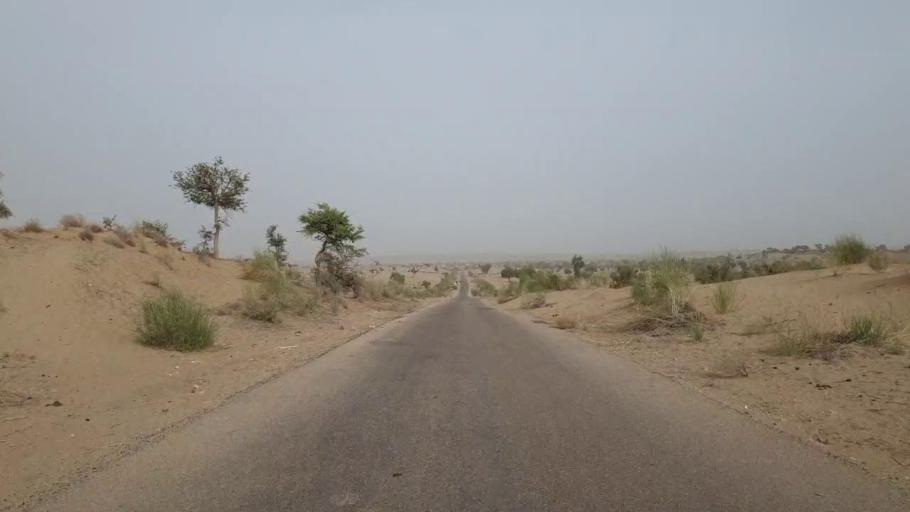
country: PK
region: Sindh
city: Islamkot
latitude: 24.5551
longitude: 70.3492
